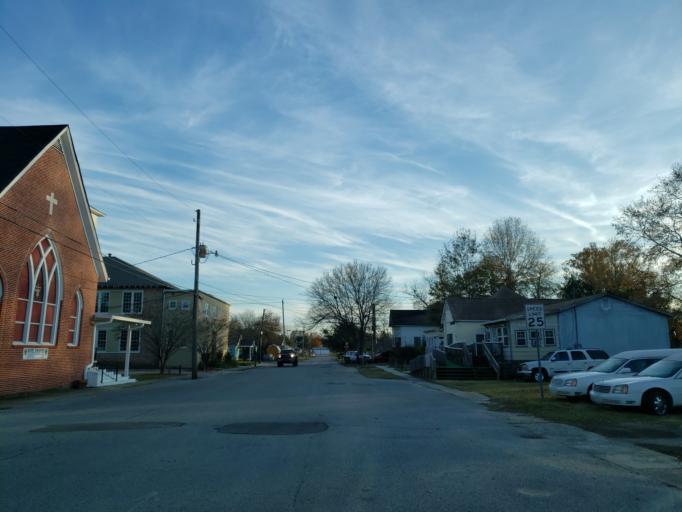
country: US
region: Mississippi
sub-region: Forrest County
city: Hattiesburg
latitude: 31.3354
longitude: -89.2915
